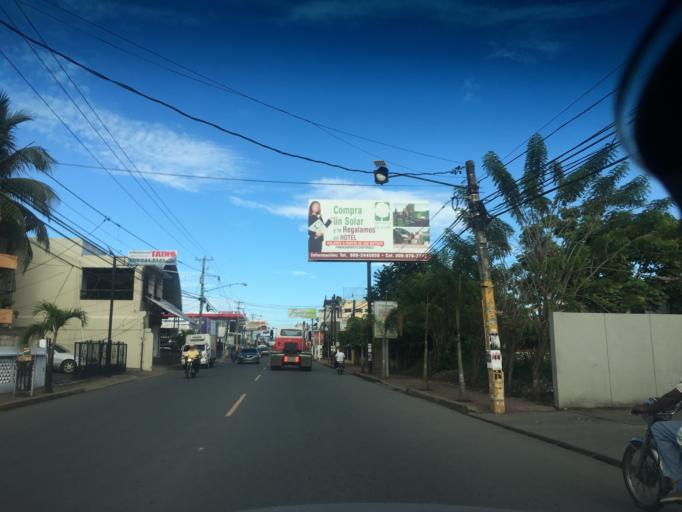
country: DO
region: Duarte
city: San Francisco de Macoris
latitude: 19.2868
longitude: -70.2712
